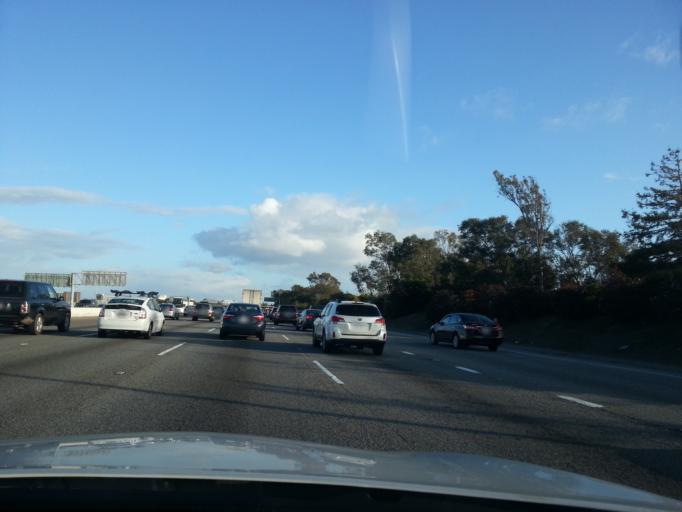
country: US
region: California
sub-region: San Mateo County
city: Millbrae
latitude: 37.6067
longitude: -122.3870
